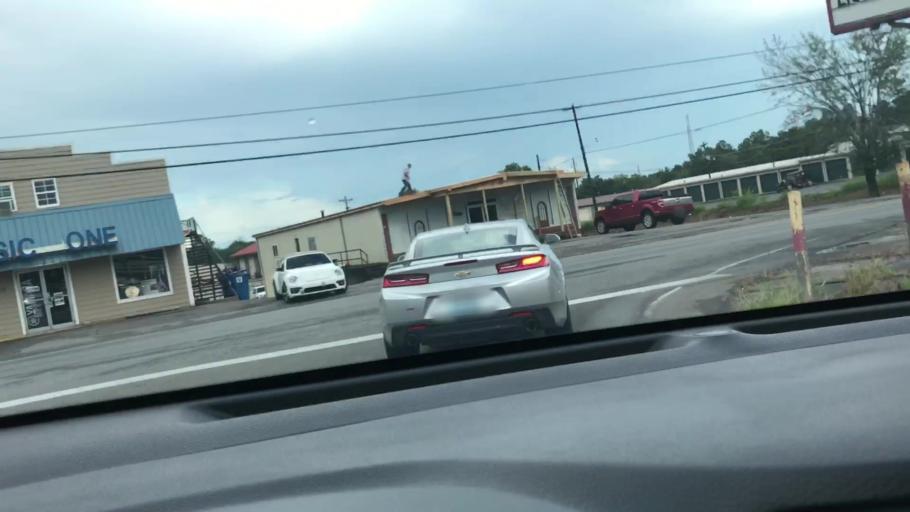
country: US
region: Kentucky
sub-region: Calloway County
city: Murray
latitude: 36.6026
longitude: -88.3029
